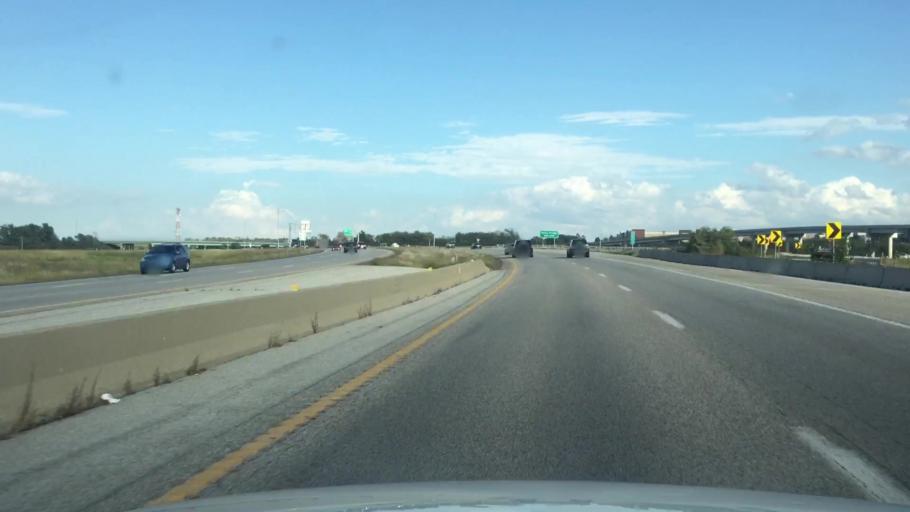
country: US
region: Missouri
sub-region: Jackson County
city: Lees Summit
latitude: 38.9337
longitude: -94.4106
